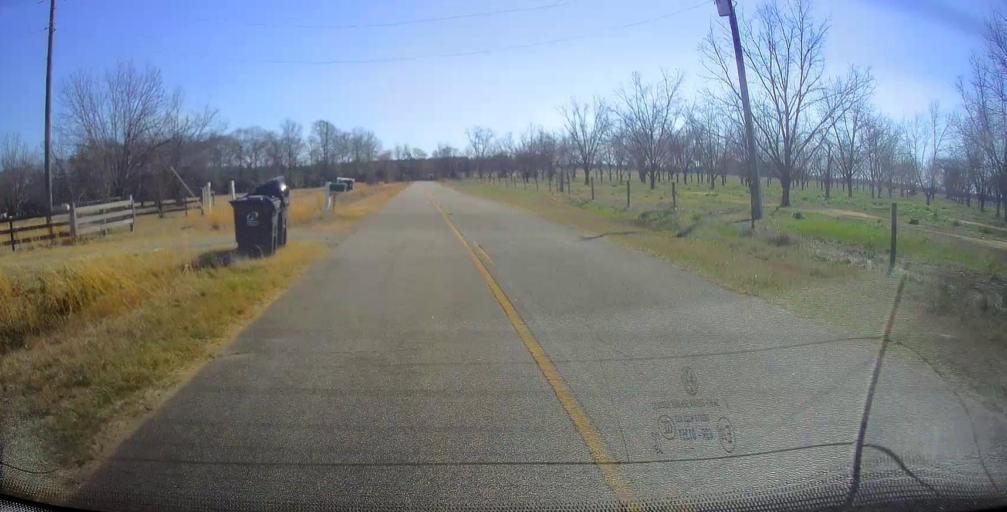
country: US
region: Georgia
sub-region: Peach County
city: Byron
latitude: 32.6259
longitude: -83.8389
